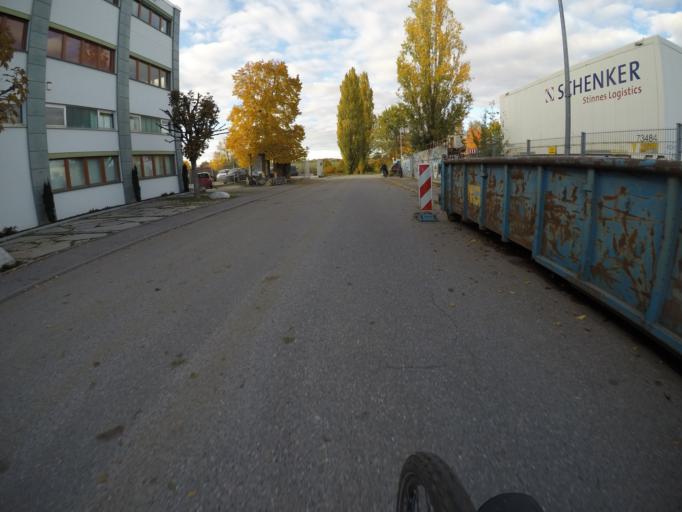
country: DE
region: Baden-Wuerttemberg
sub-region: Regierungsbezirk Stuttgart
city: Leinfelden-Echterdingen
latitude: 48.6741
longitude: 9.1825
